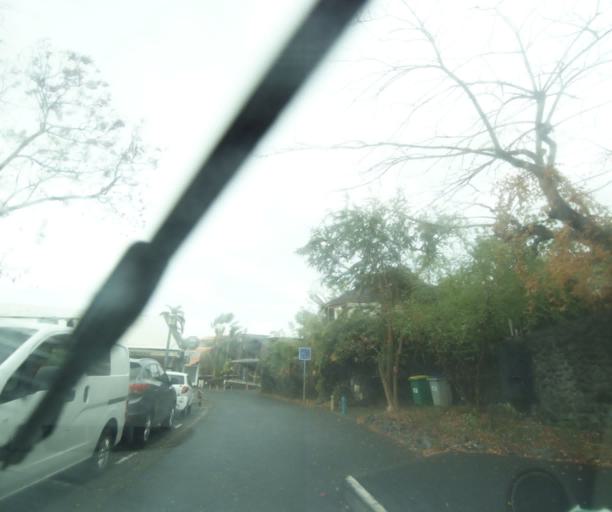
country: RE
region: Reunion
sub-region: Reunion
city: Saint-Paul
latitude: -21.0459
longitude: 55.2563
